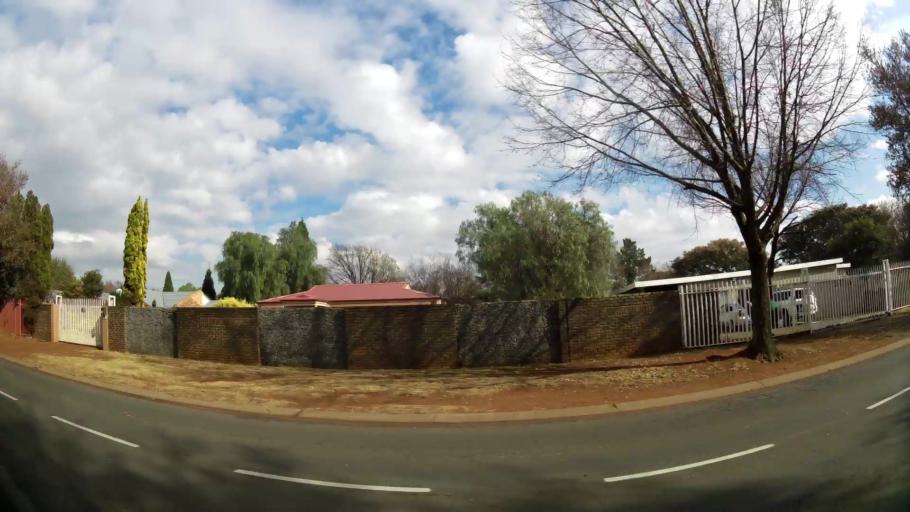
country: ZA
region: Gauteng
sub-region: Sedibeng District Municipality
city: Meyerton
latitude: -26.5526
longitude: 28.0326
